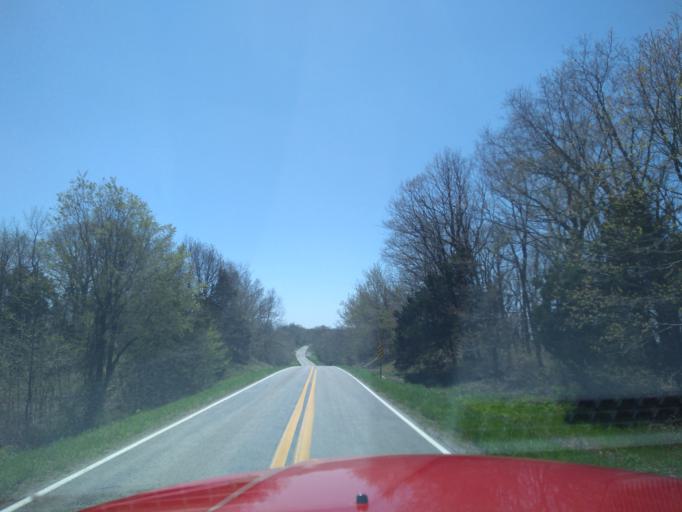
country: US
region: Arkansas
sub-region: Washington County
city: West Fork
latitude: 35.8180
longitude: -94.2587
